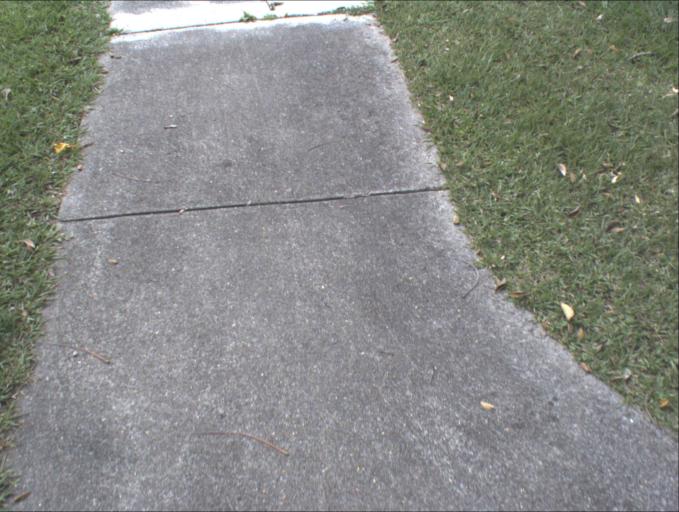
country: AU
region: Queensland
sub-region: Logan
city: Waterford West
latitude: -27.6878
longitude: 153.1221
